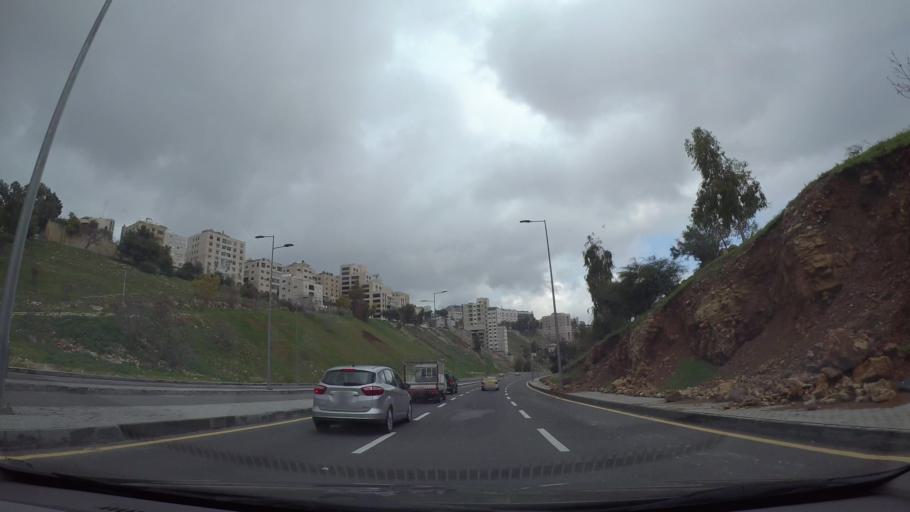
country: JO
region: Amman
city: Amman
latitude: 31.9516
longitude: 35.8985
